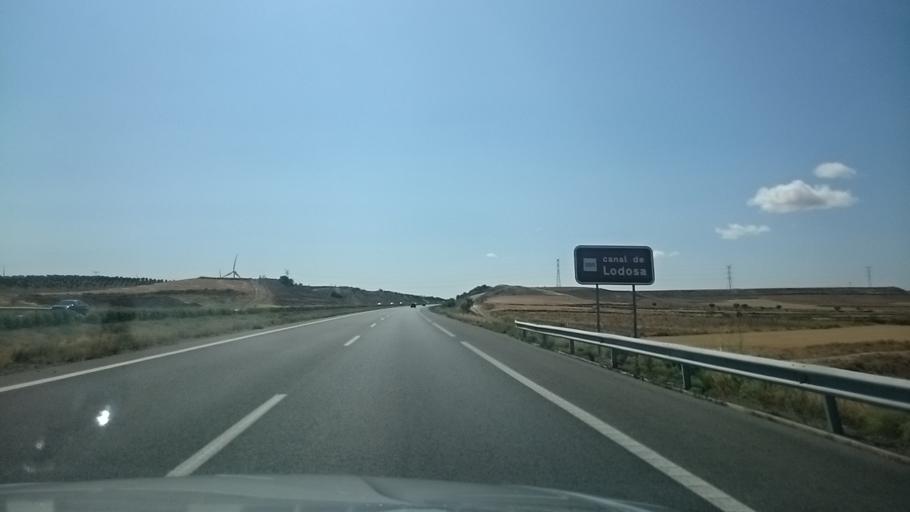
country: ES
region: Aragon
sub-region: Provincia de Zaragoza
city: Mallen
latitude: 41.8852
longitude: -1.4134
